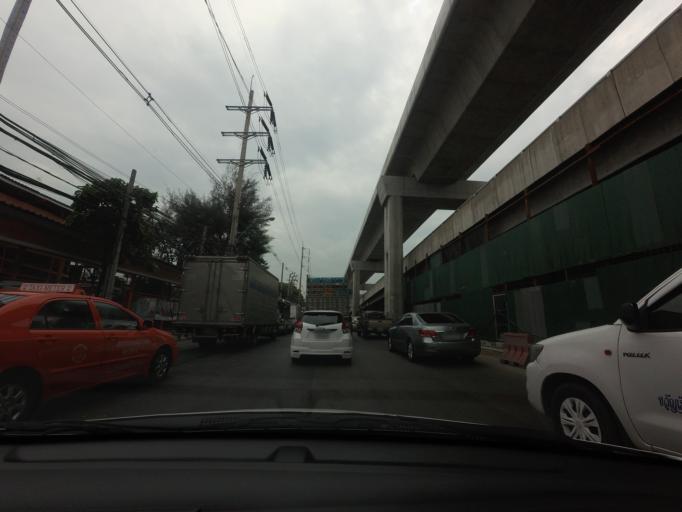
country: TH
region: Samut Prakan
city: Samut Prakan
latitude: 13.5946
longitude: 100.6077
